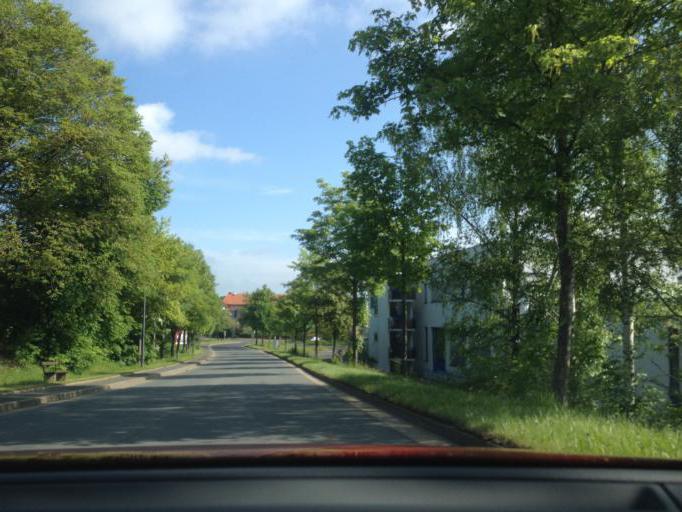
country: DE
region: Bavaria
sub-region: Upper Franconia
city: Marktredwitz
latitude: 50.0105
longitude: 12.0887
